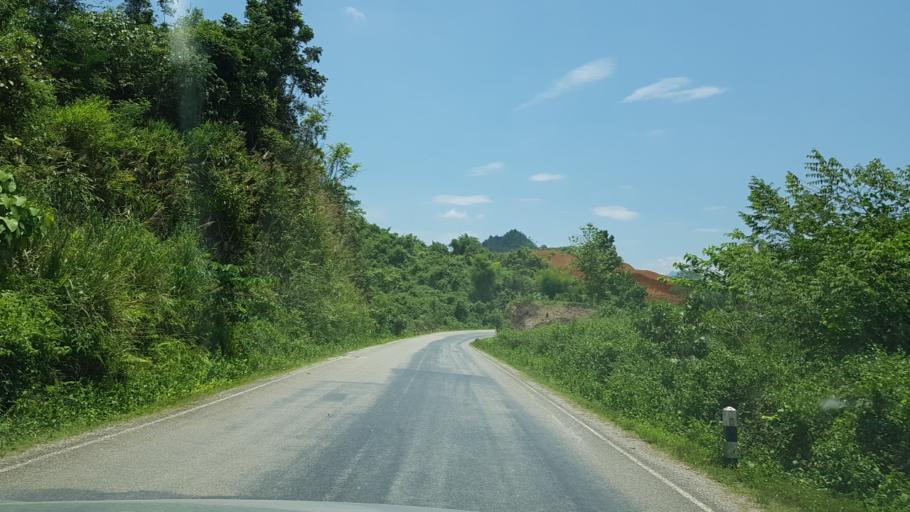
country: LA
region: Vientiane
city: Muang Kasi
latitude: 19.2706
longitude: 102.2125
